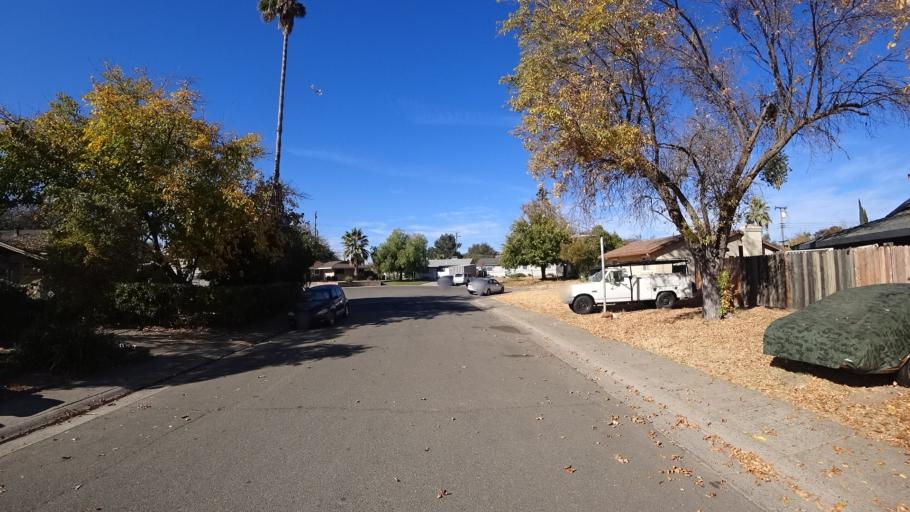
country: US
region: California
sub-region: Sacramento County
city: Antelope
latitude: 38.7157
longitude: -121.3079
